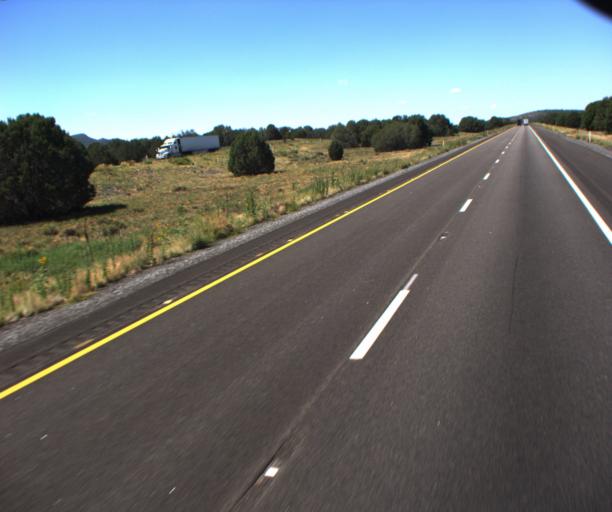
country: US
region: Arizona
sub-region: Mohave County
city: Peach Springs
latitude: 35.2143
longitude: -113.2584
